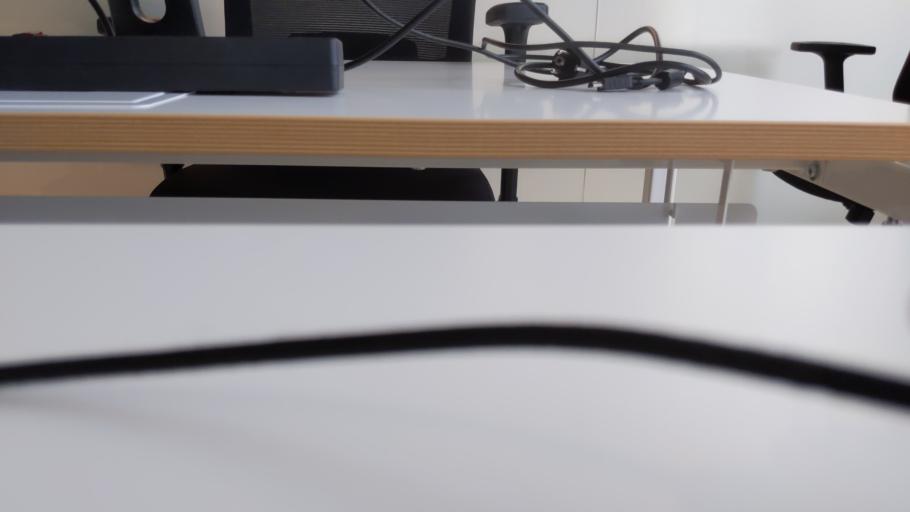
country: RU
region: Moskovskaya
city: Shevlyakovo
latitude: 56.4215
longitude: 37.0052
